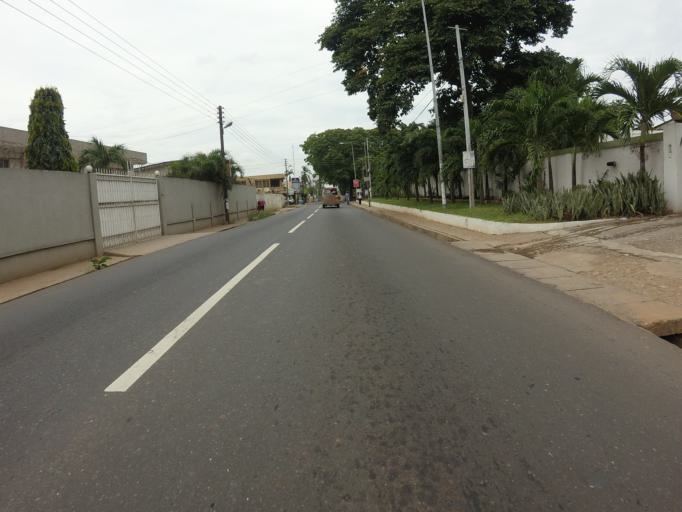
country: GH
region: Greater Accra
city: Dome
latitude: 5.5991
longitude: -0.2268
